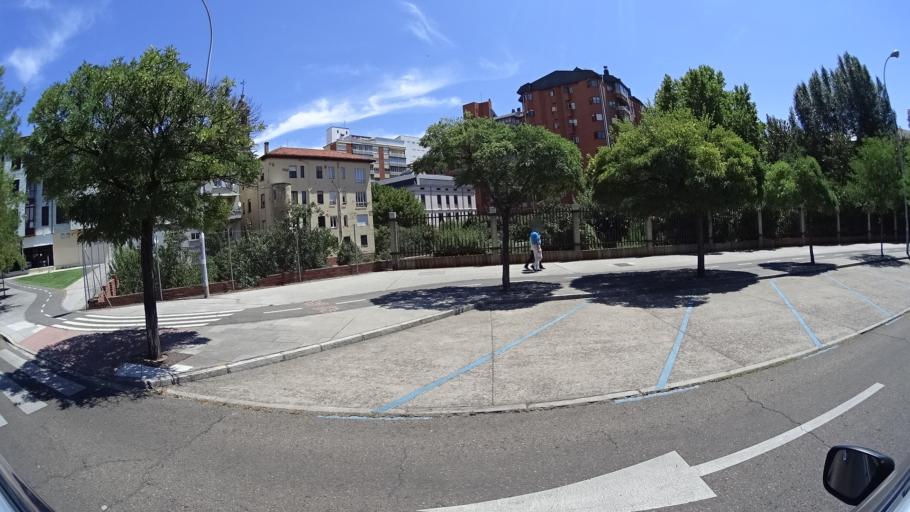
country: ES
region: Castille and Leon
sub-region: Provincia de Leon
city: Leon
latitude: 42.6035
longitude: -5.5776
